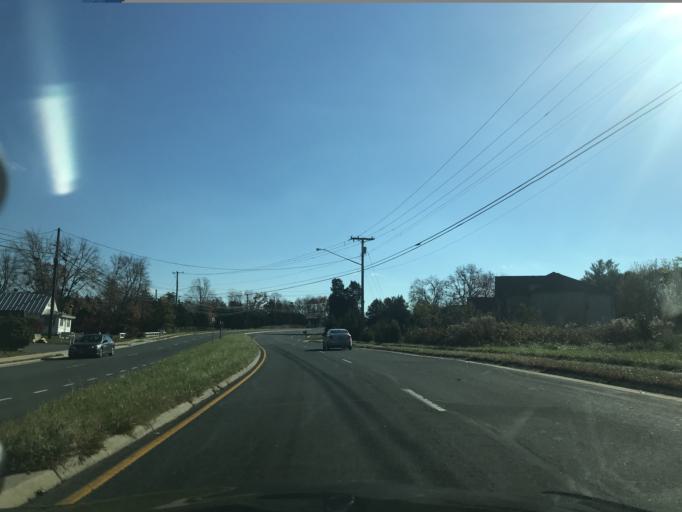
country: US
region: Virginia
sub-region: Fairfax County
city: Oak Hill
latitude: 38.9016
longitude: -77.3821
